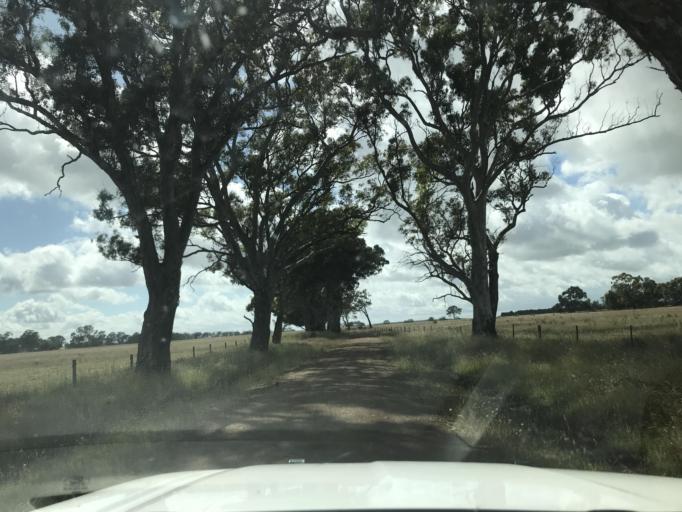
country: AU
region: South Australia
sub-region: Wattle Range
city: Penola
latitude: -37.2177
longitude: 141.3369
